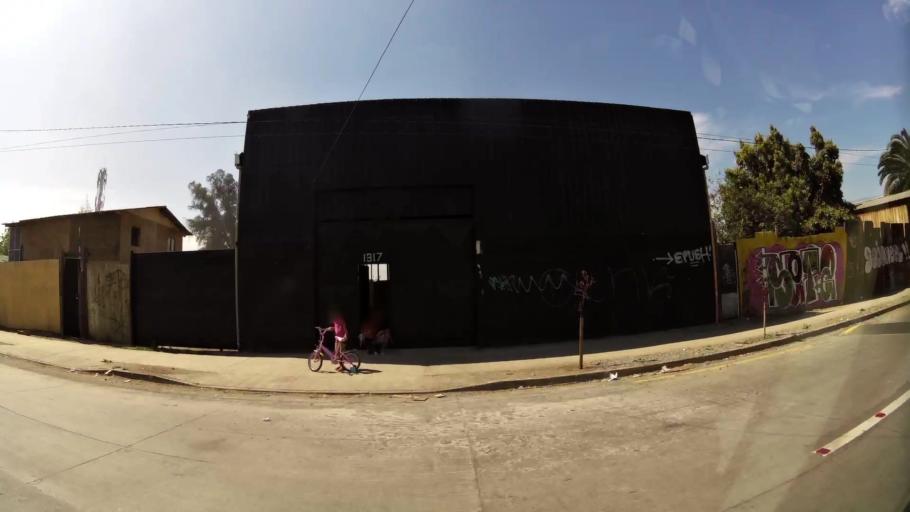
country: CL
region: Santiago Metropolitan
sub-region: Provincia de Santiago
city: Lo Prado
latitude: -33.4061
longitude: -70.7198
